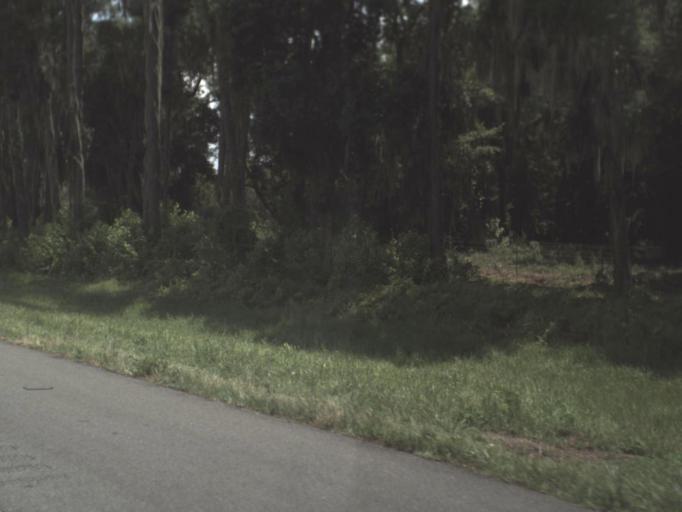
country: US
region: Florida
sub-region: Hamilton County
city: Jasper
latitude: 30.4343
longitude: -82.9128
